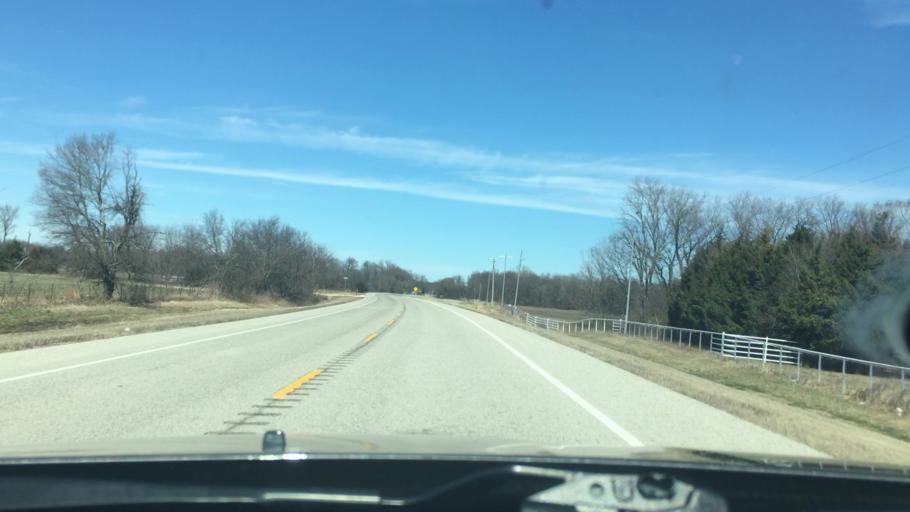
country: US
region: Oklahoma
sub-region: Murray County
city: Sulphur
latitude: 34.3855
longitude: -96.9509
